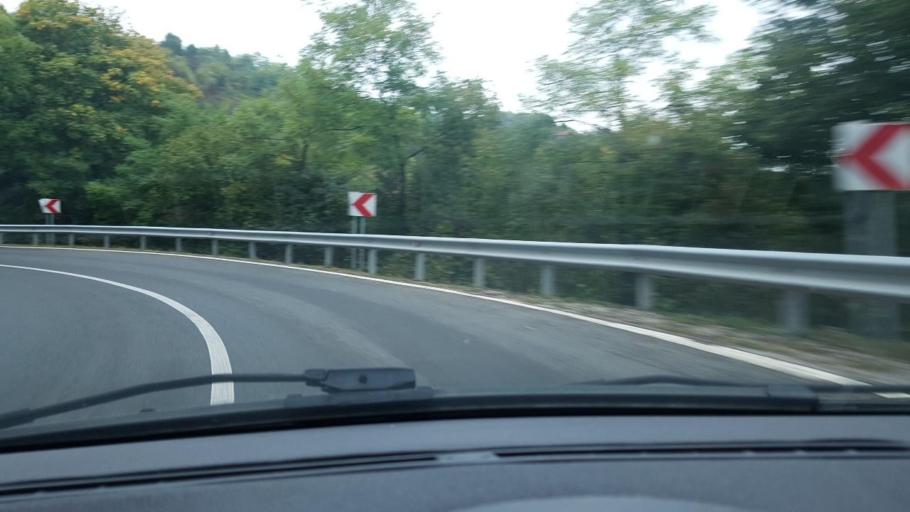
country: HR
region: Krapinsko-Zagorska
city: Marija Bistrica
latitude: 45.9746
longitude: 16.1026
